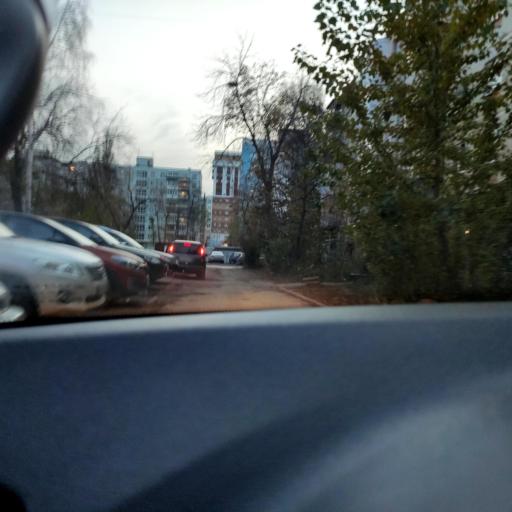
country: RU
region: Samara
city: Samara
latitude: 53.2433
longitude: 50.2136
